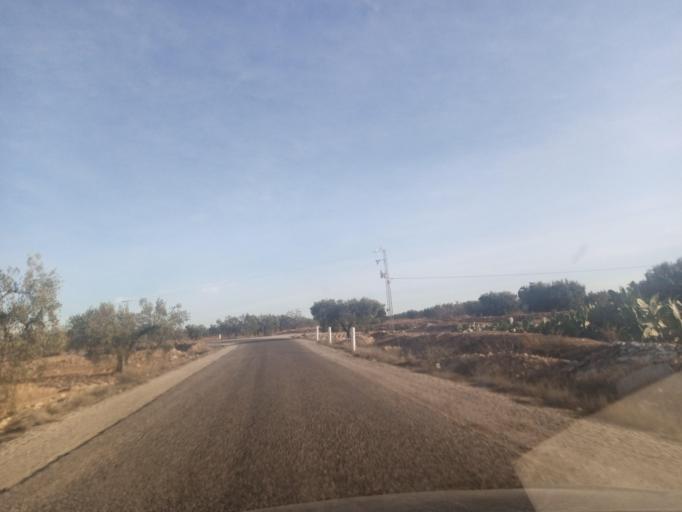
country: TN
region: Safaqis
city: Bi'r `Ali Bin Khalifah
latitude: 34.8879
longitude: 10.1812
